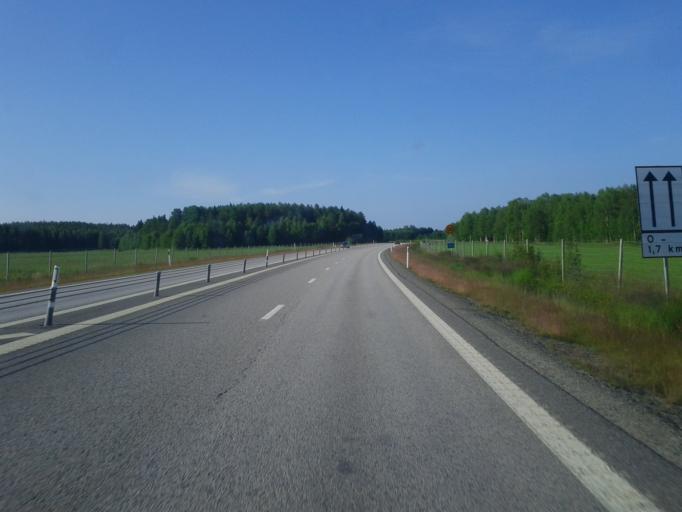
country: SE
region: Vaesterbotten
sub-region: Robertsfors Kommun
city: Robertsfors
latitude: 64.1397
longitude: 20.8948
